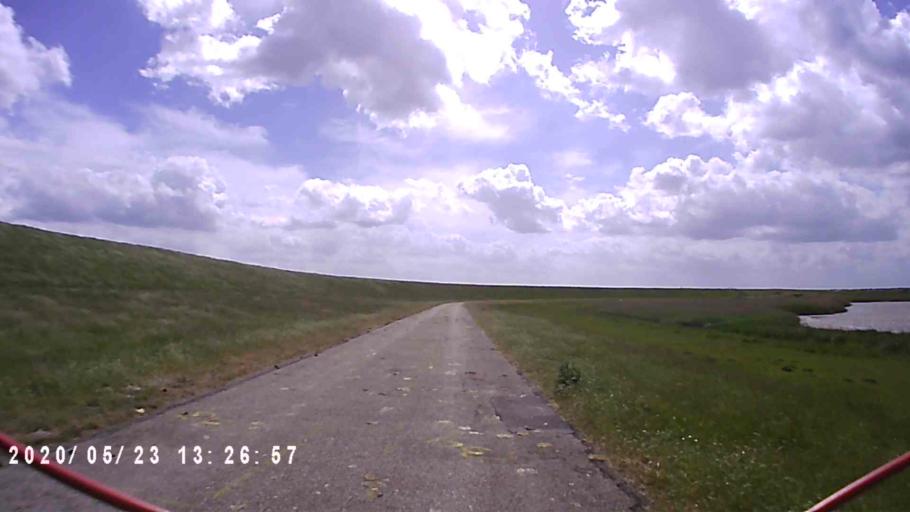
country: NL
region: Groningen
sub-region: Gemeente  Oldambt
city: Winschoten
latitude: 53.2831
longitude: 7.0838
